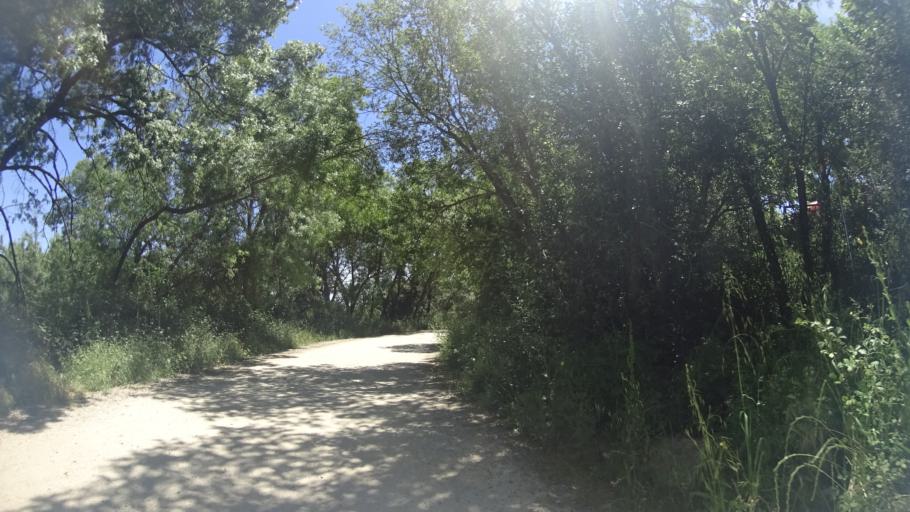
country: ES
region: Madrid
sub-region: Provincia de Madrid
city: Navalquejigo
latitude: 40.6103
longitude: -4.0323
